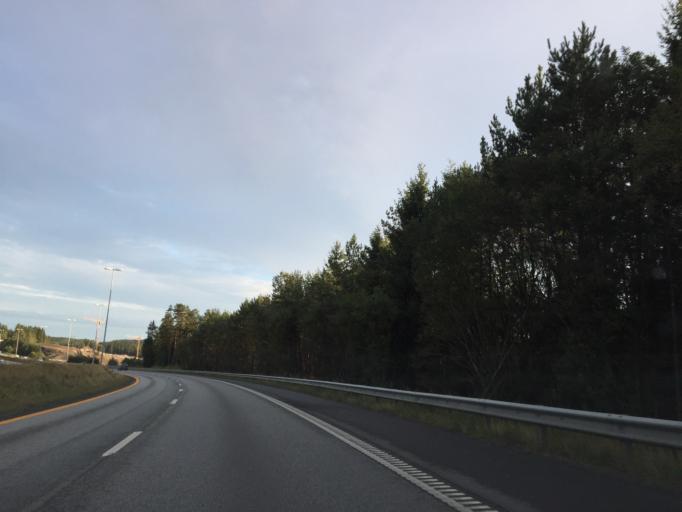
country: NO
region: Akershus
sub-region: Oppegard
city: Kolbotn
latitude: 59.8132
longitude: 10.8400
